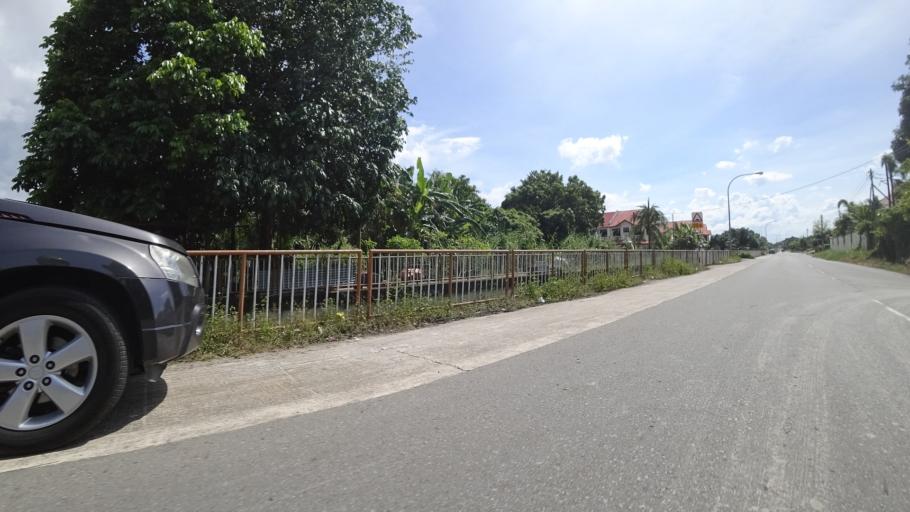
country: BN
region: Brunei and Muara
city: Bandar Seri Begawan
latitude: 4.8904
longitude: 114.8483
